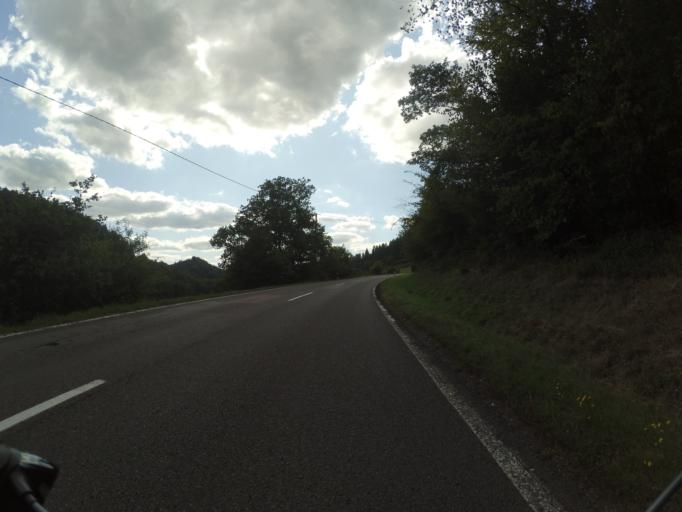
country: DE
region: Rheinland-Pfalz
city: Budlich
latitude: 49.7791
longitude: 6.8952
